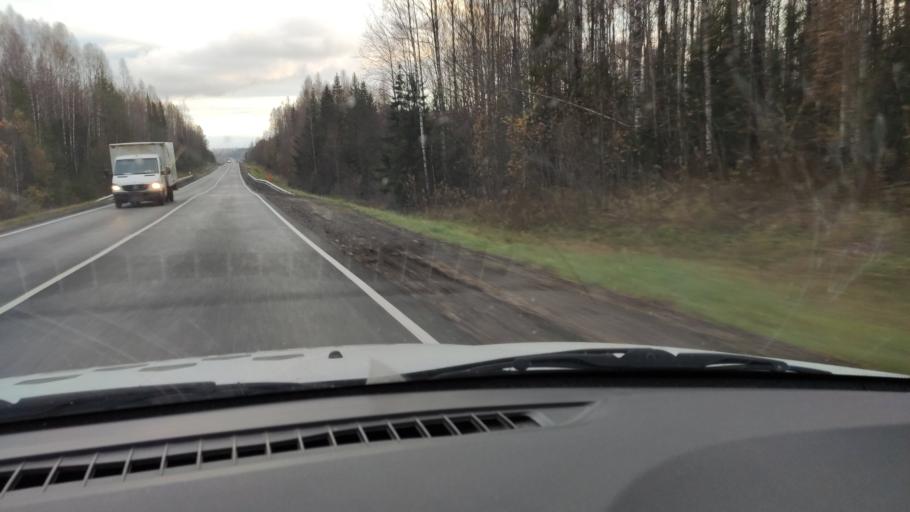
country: RU
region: Kirov
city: Omutninsk
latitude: 58.7405
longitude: 52.0676
